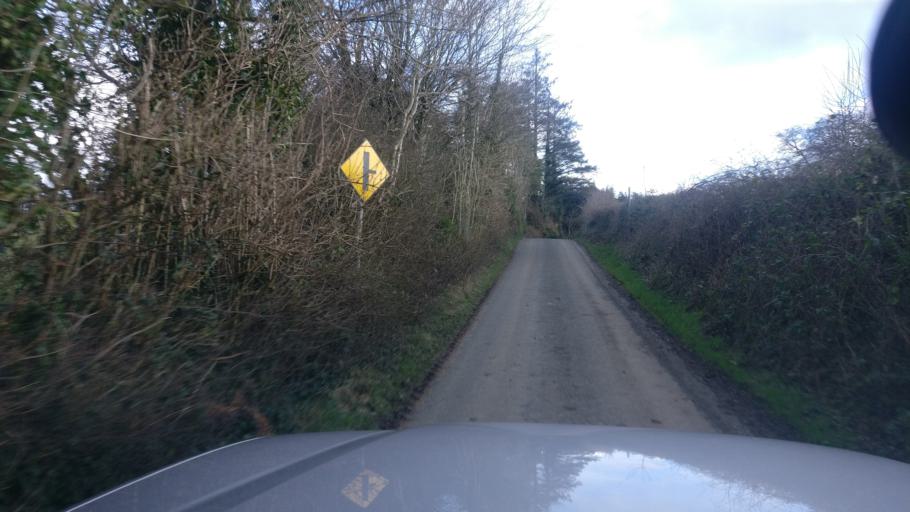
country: IE
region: Connaught
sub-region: County Galway
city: Loughrea
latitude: 53.1818
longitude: -8.4263
